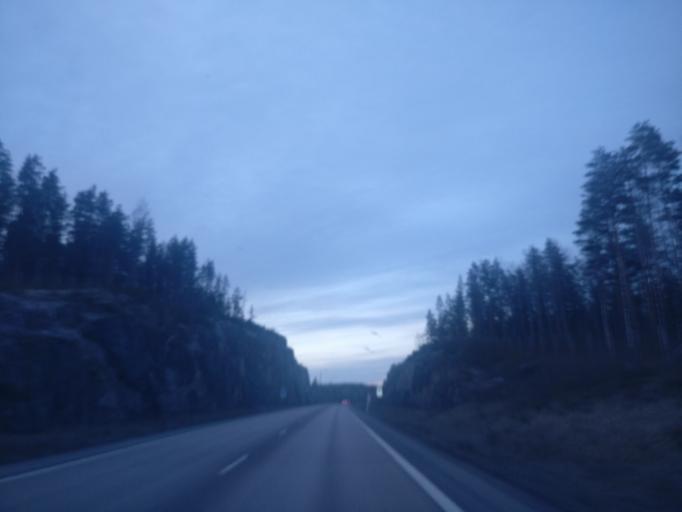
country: FI
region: Central Finland
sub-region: Jyvaeskylae
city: Saeynaetsalo
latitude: 62.2051
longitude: 25.8902
